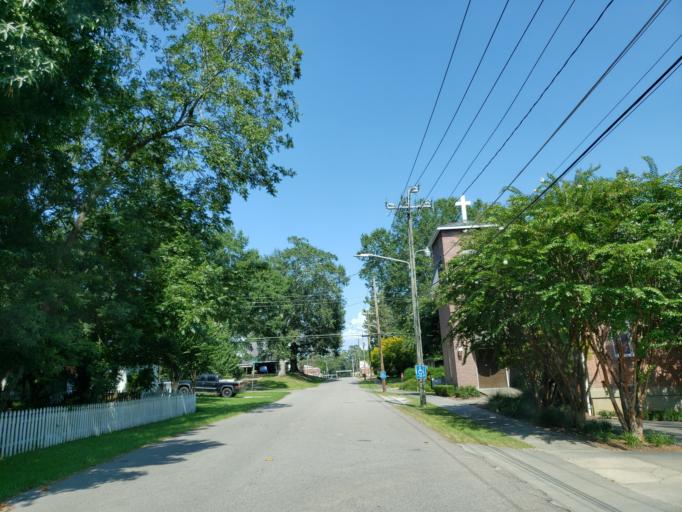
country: US
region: Mississippi
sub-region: Lamar County
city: Sumrall
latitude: 31.4175
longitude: -89.5453
